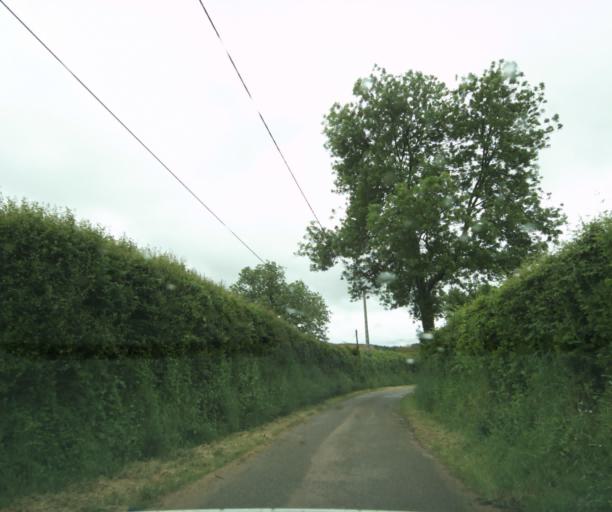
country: FR
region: Bourgogne
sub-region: Departement de Saone-et-Loire
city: Charolles
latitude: 46.4404
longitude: 4.4246
